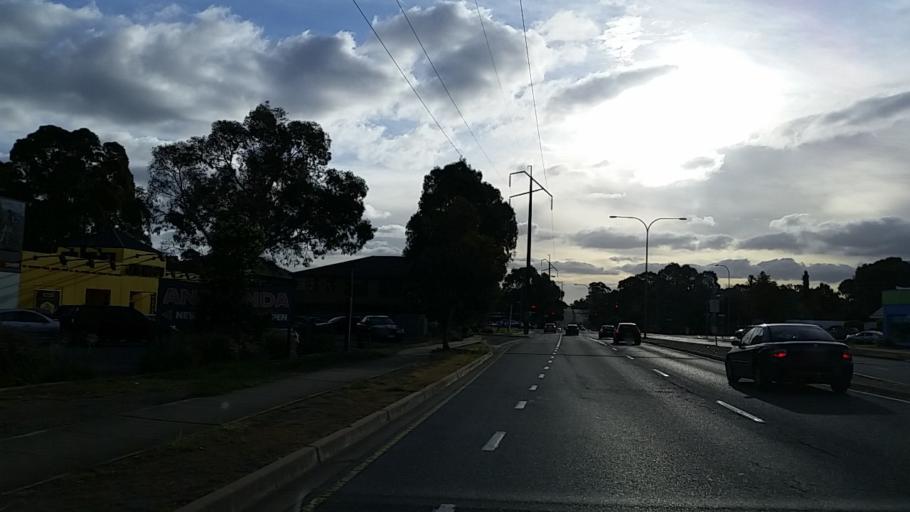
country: AU
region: South Australia
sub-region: Tea Tree Gully
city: Modbury
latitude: -34.8337
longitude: 138.6844
